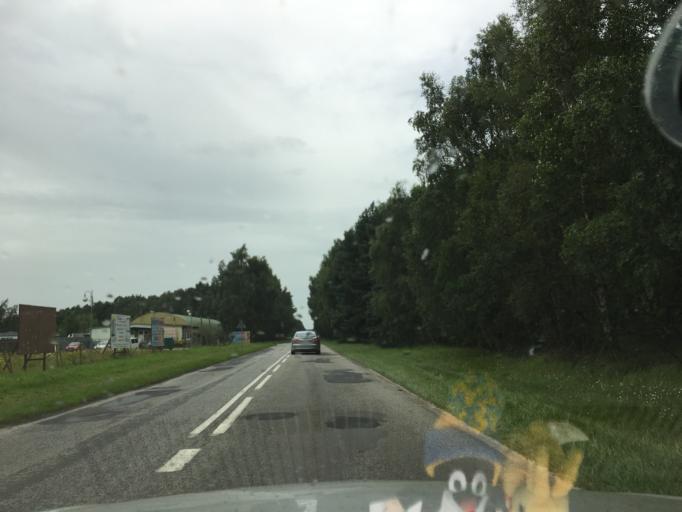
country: PL
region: West Pomeranian Voivodeship
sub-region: Powiat gryficki
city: Pobierowo
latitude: 54.0476
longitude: 14.9260
